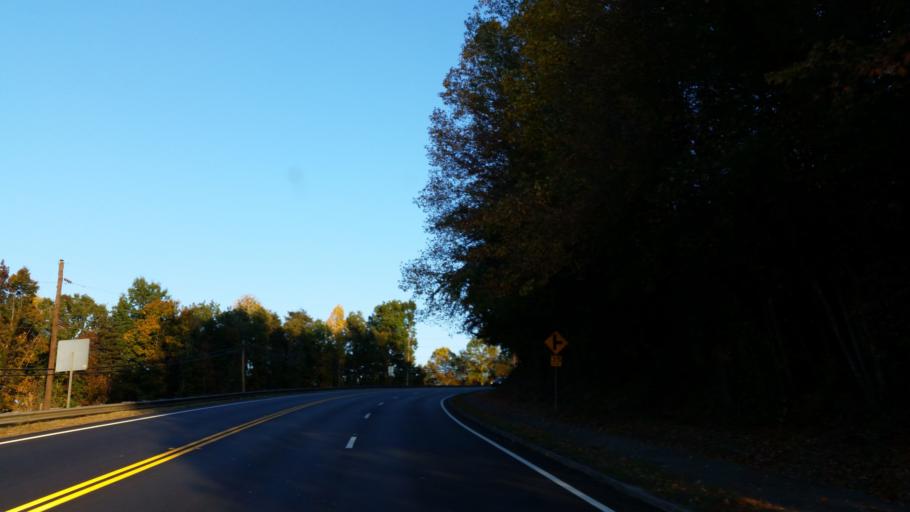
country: US
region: Georgia
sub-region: Lumpkin County
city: Dahlonega
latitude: 34.5267
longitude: -83.9782
